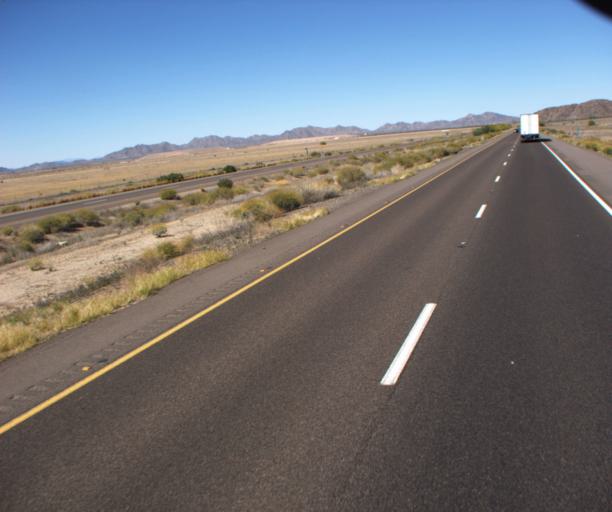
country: US
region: Arizona
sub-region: Maricopa County
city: Gila Bend
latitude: 33.1465
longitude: -112.6499
